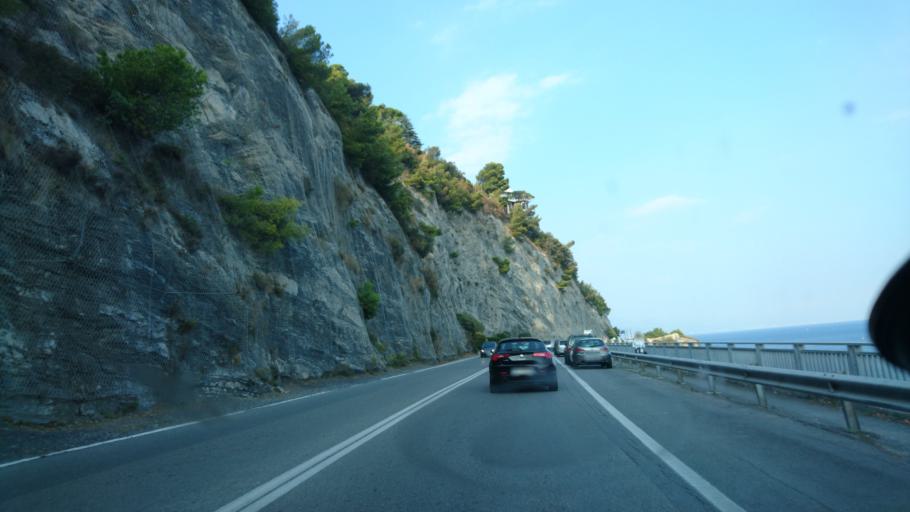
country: IT
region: Liguria
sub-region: Provincia di Savona
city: Bergeggi
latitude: 44.2391
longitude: 8.4425
